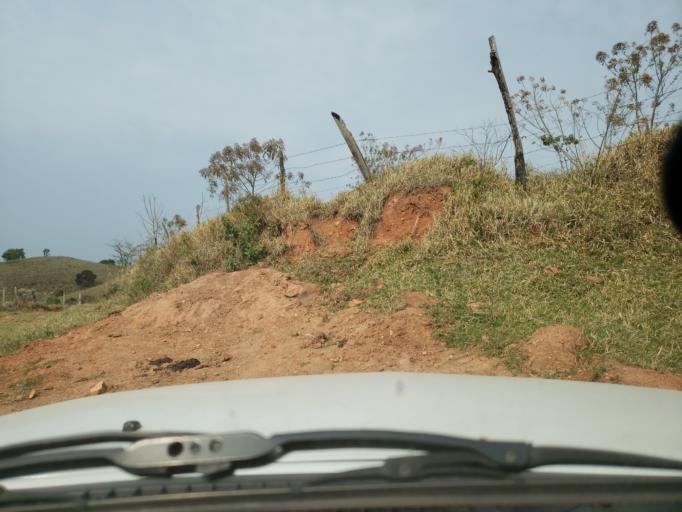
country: BR
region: Minas Gerais
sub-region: Jacutinga
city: Jacutinga
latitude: -22.3424
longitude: -46.5860
